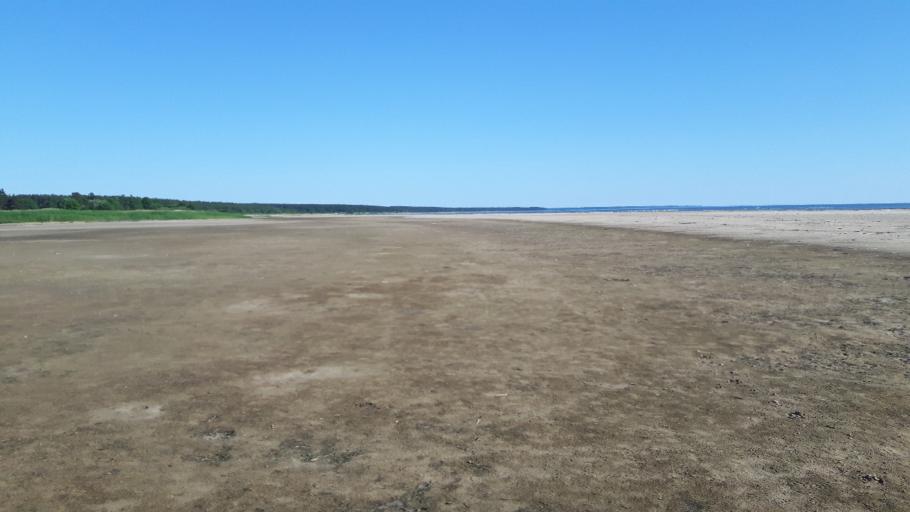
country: LV
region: Salacgrivas
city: Salacgriva
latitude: 57.6999
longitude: 24.3421
